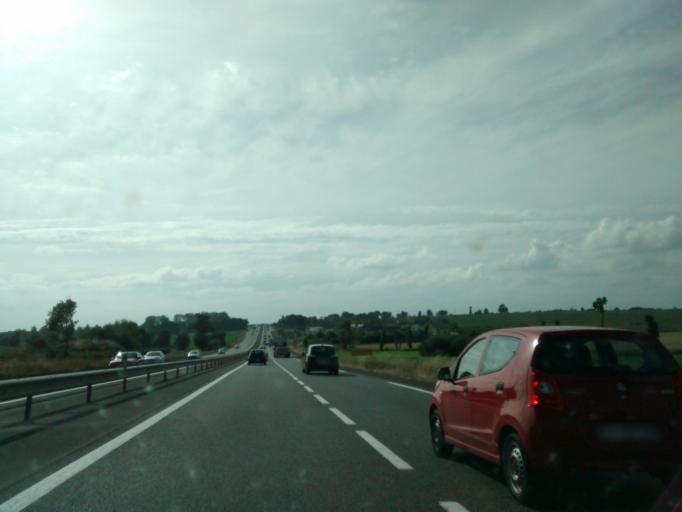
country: FR
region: Brittany
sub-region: Departement d'Ille-et-Vilaine
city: Saint-Gilles
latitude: 48.1636
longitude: -1.8615
